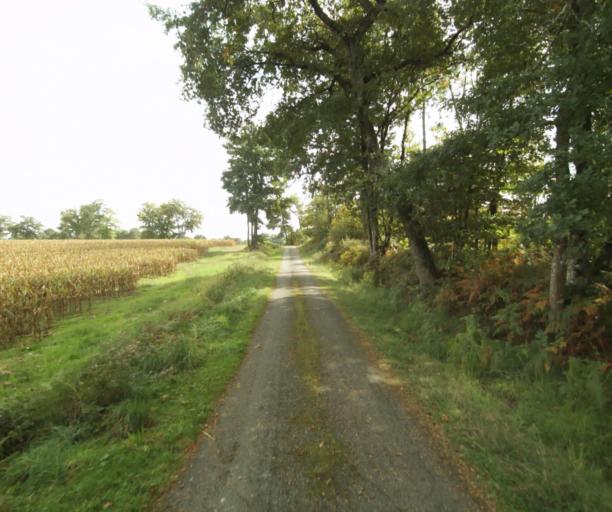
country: FR
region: Midi-Pyrenees
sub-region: Departement du Gers
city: Eauze
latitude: 43.8274
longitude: 0.0984
